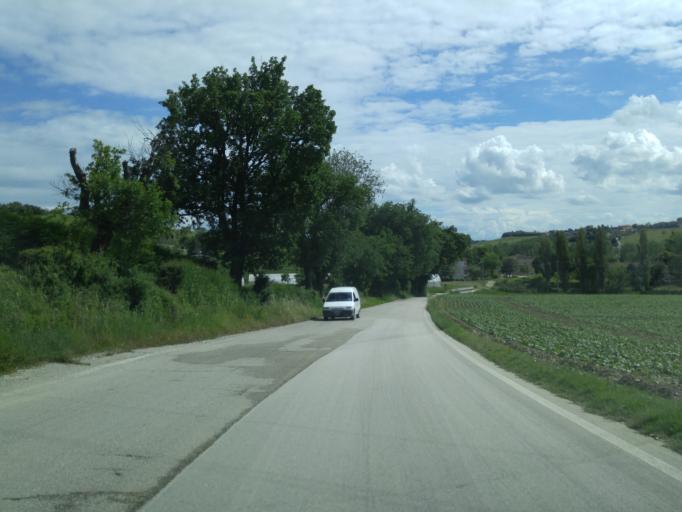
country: IT
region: The Marches
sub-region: Provincia di Pesaro e Urbino
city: Bellocchi
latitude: 43.7927
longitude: 13.0422
